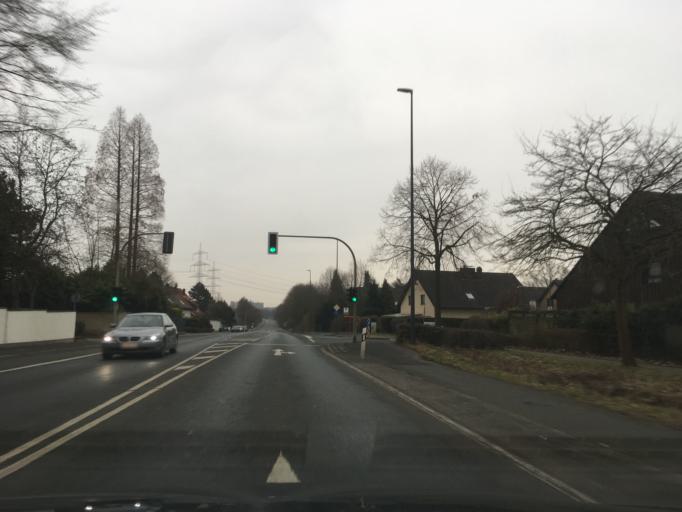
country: DE
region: North Rhine-Westphalia
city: Herten
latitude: 51.5981
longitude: 7.1039
